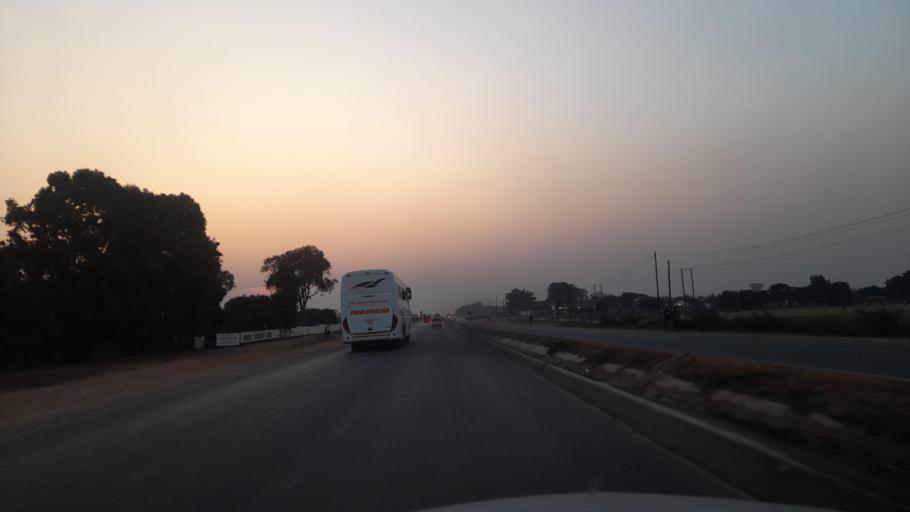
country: ZM
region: Copperbelt
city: Kitwe
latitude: -12.7733
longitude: 28.1876
